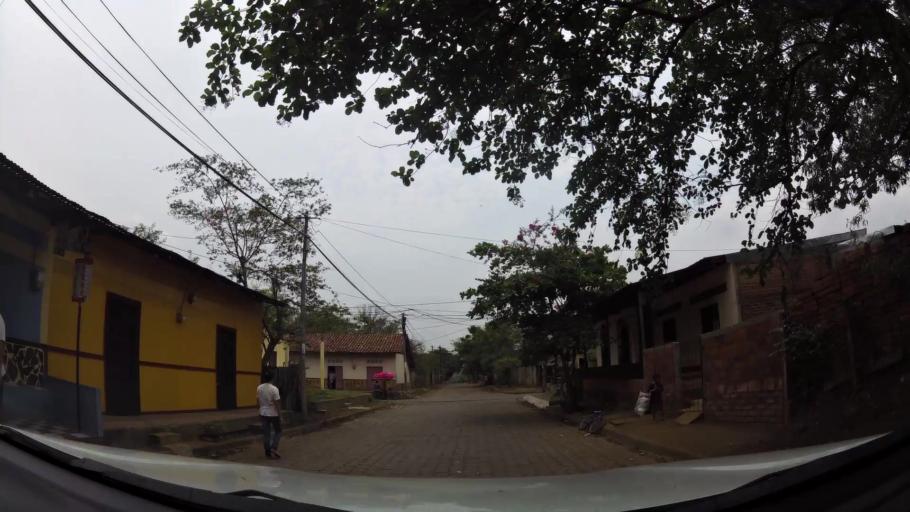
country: NI
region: Leon
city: Leon
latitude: 12.4397
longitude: -86.8895
